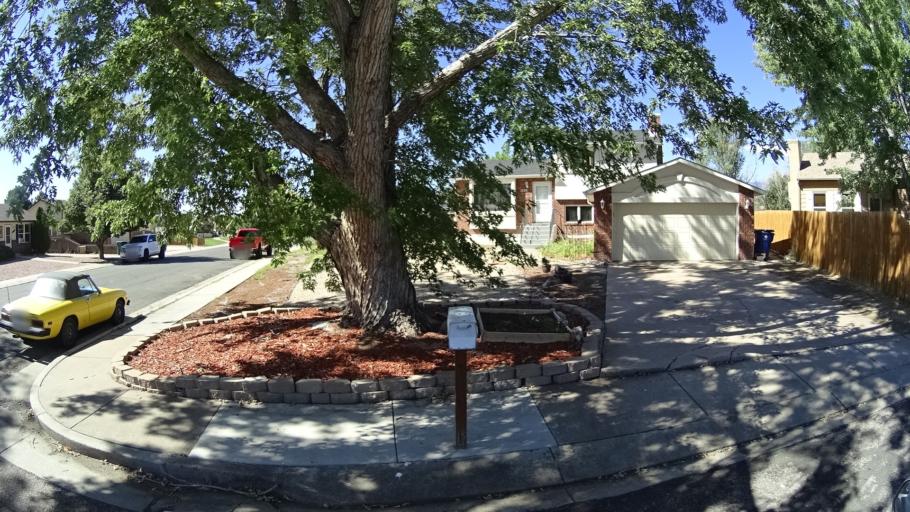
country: US
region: Colorado
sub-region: El Paso County
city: Cimarron Hills
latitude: 38.8136
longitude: -104.7344
